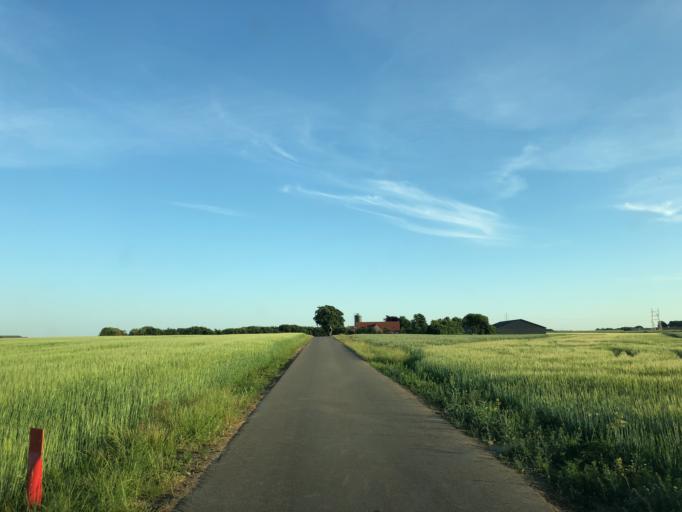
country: DK
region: Central Jutland
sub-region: Struer Kommune
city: Struer
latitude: 56.4767
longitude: 8.5617
